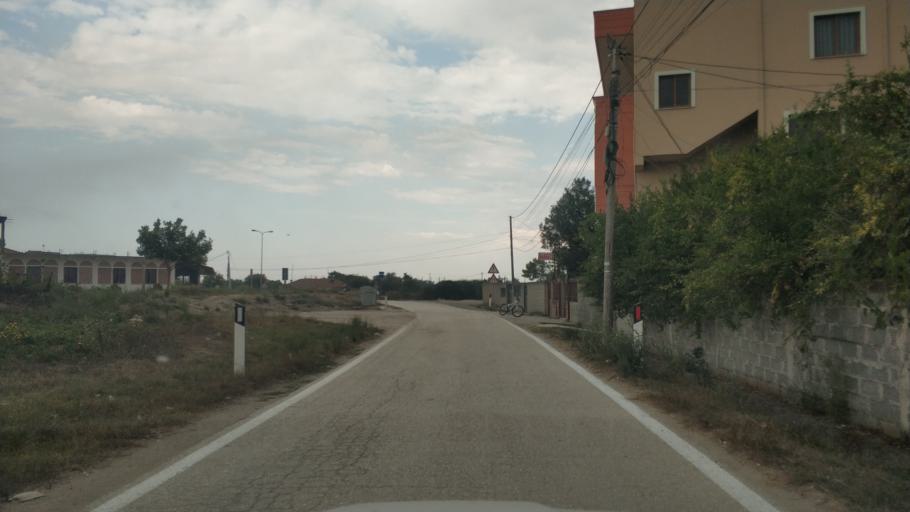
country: AL
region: Fier
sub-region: Rrethi i Fierit
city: Dermenas
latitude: 40.7278
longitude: 19.4688
